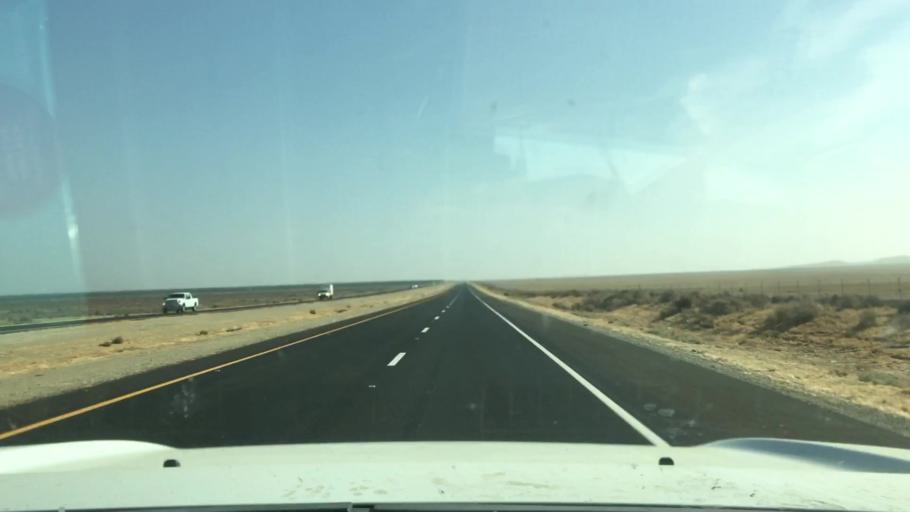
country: US
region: California
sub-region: Kern County
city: Lost Hills
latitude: 35.6265
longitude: -119.9900
